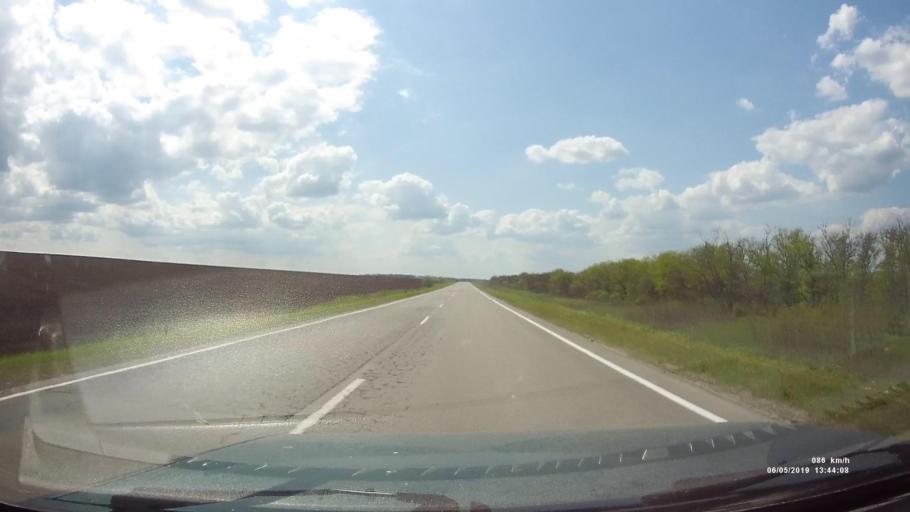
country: RU
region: Rostov
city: Melikhovskaya
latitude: 47.6589
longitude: 40.6243
